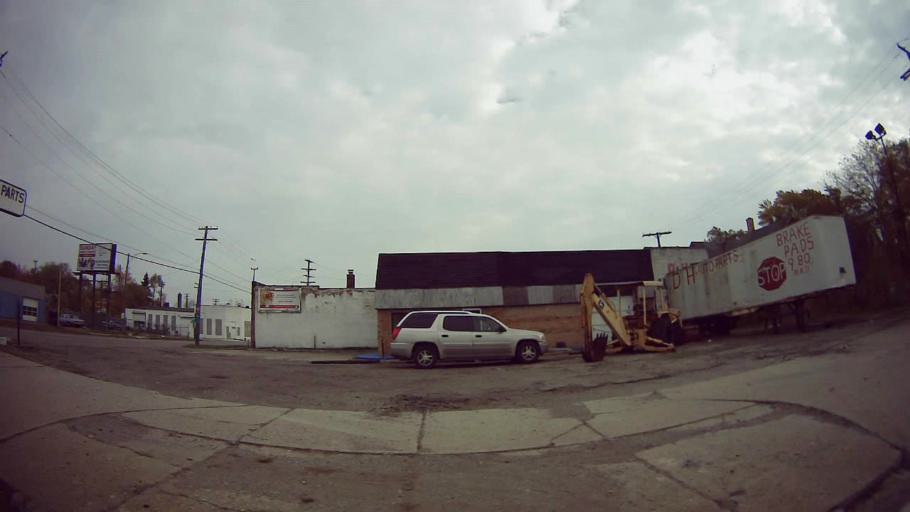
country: US
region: Michigan
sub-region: Wayne County
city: Hamtramck
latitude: 42.4189
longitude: -83.0424
